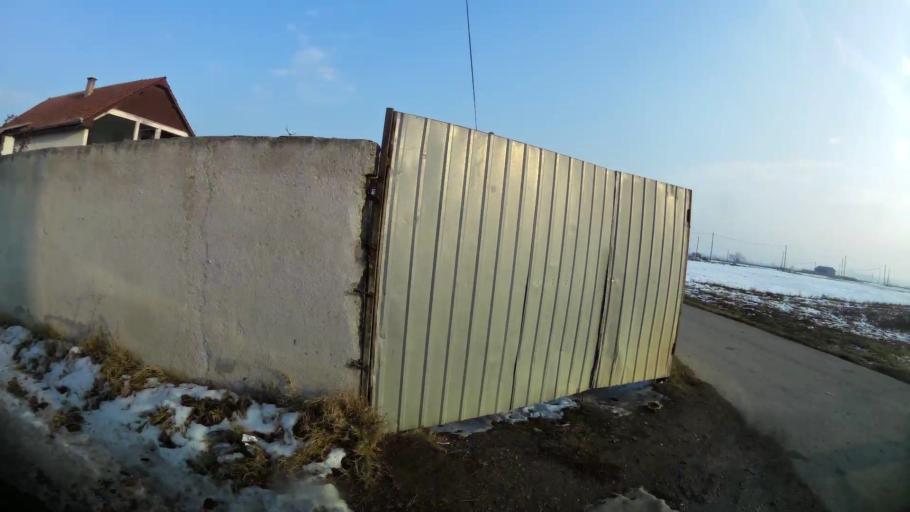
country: MK
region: Aracinovo
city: Arachinovo
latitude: 42.0120
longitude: 21.5288
